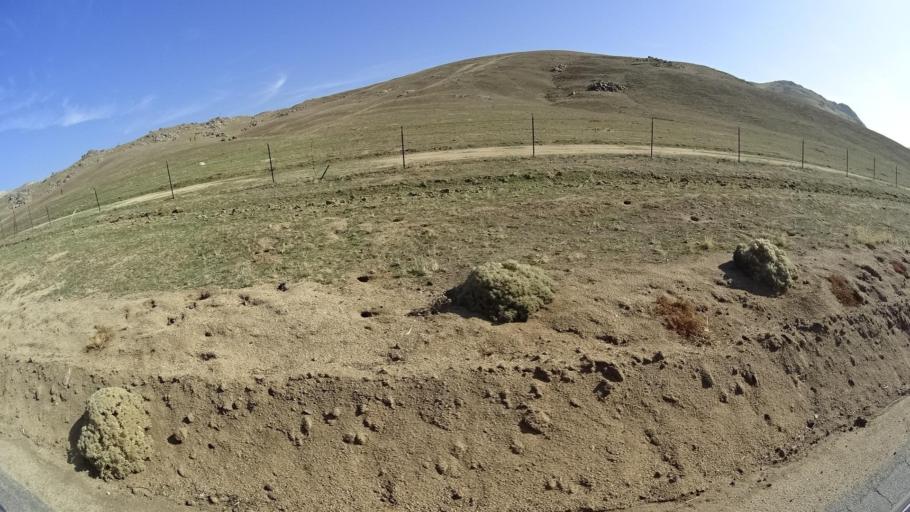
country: US
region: California
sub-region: Kern County
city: Oildale
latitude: 35.4689
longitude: -118.8290
